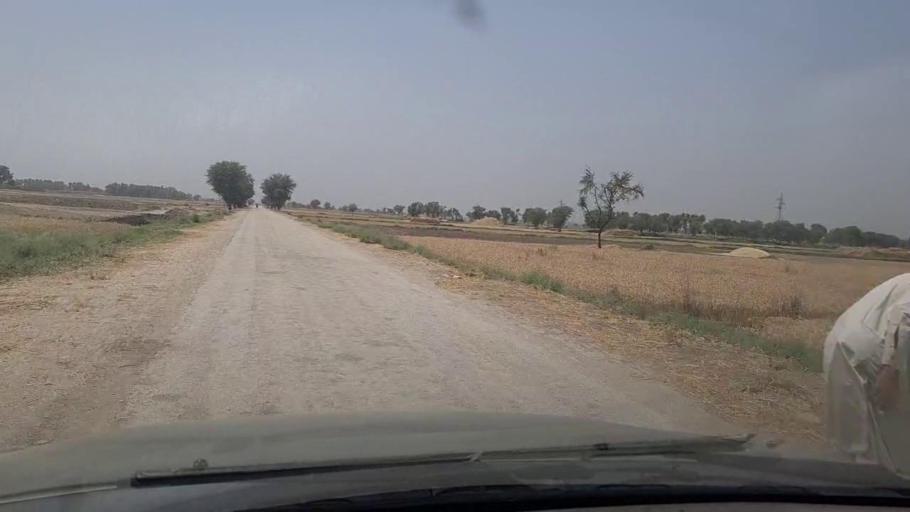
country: PK
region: Sindh
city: Ratodero
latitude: 27.7950
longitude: 68.2463
